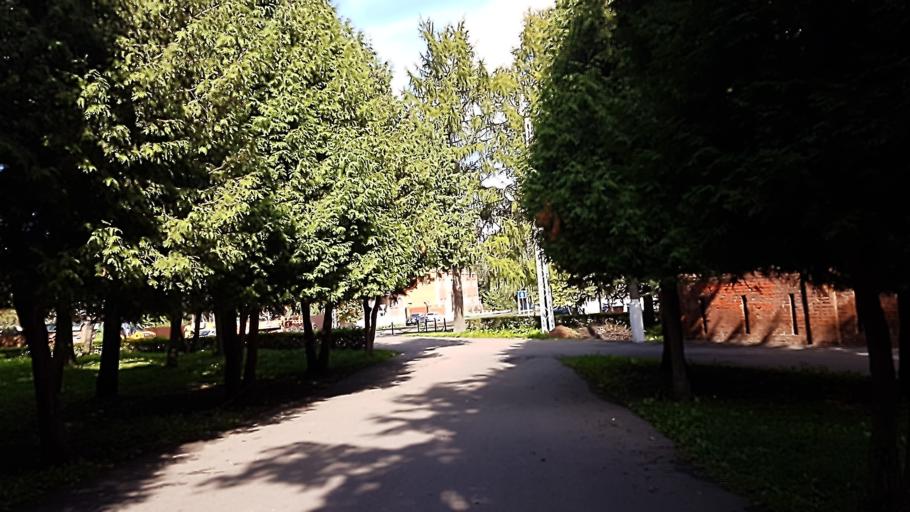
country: RU
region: Moskovskaya
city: Kolomna
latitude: 55.0952
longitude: 38.7707
